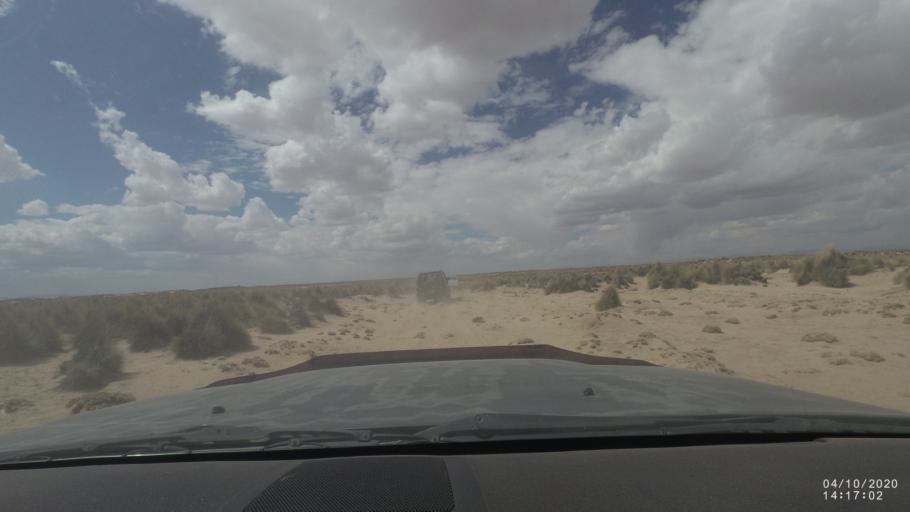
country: BO
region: Oruro
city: Poopo
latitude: -18.6886
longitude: -67.4518
